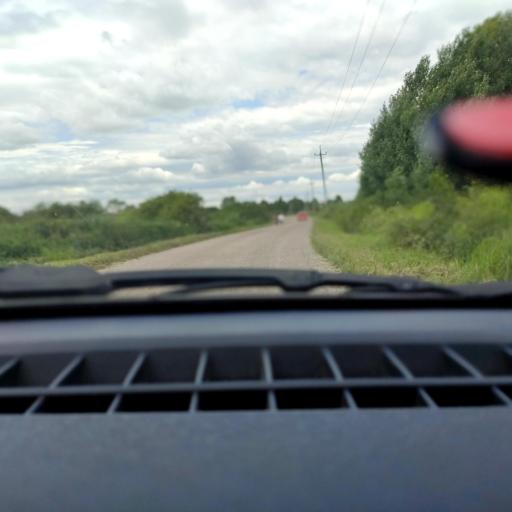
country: RU
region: Bashkortostan
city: Kabakovo
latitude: 54.7278
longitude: 56.2046
